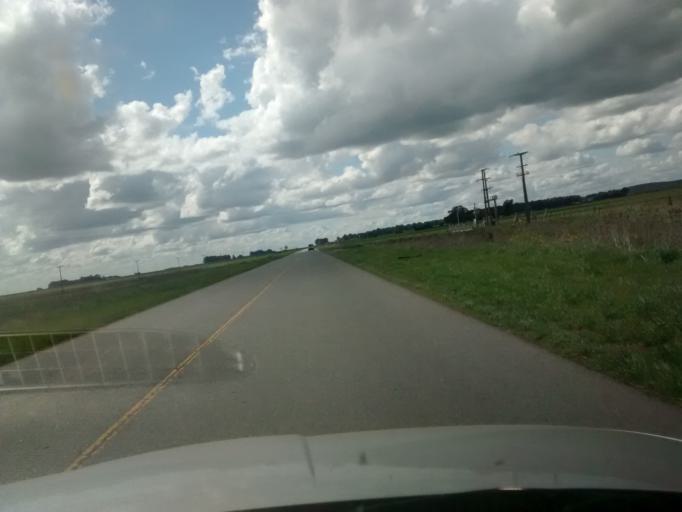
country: AR
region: Buenos Aires
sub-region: Partido de Loberia
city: Loberia
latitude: -37.7012
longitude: -58.7253
